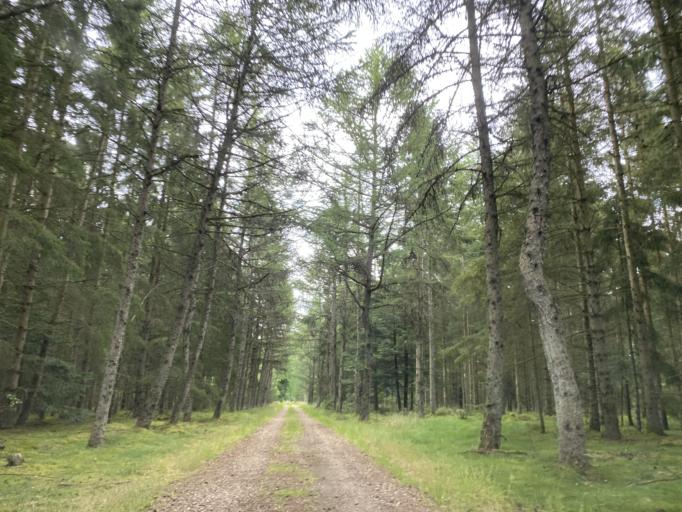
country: DK
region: Central Jutland
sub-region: Viborg Kommune
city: Bjerringbro
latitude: 56.2688
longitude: 9.6507
